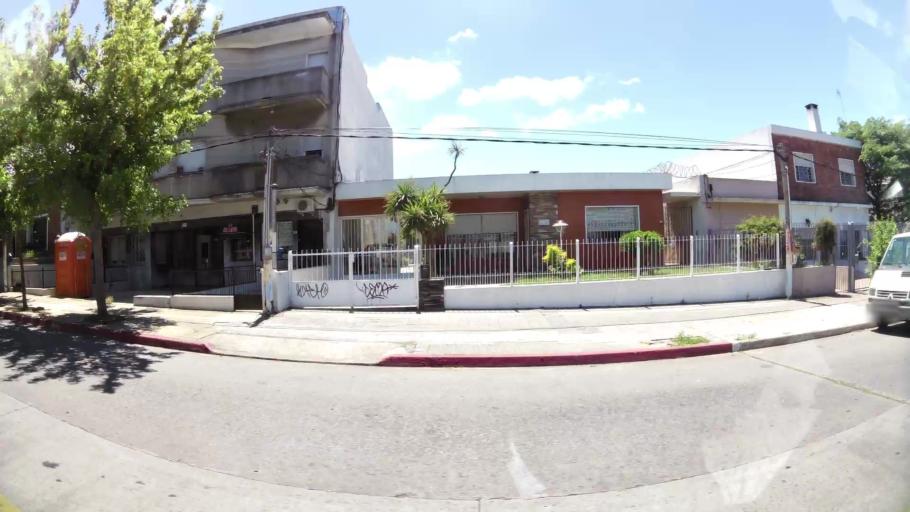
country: UY
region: Montevideo
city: Montevideo
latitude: -34.8927
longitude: -56.1245
